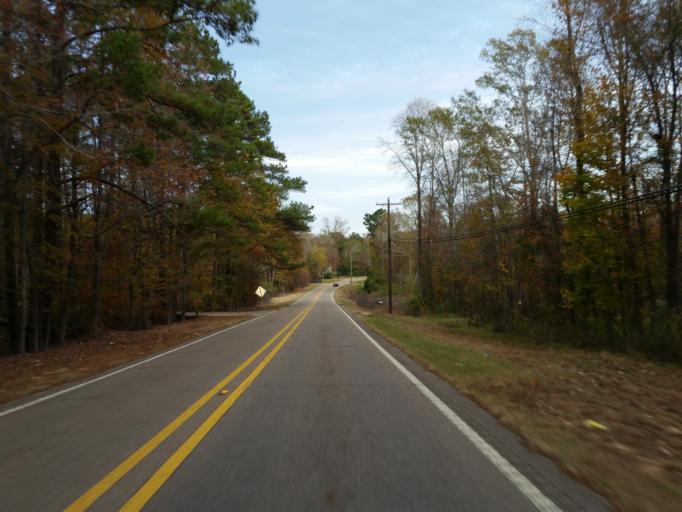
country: US
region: Mississippi
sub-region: Lauderdale County
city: Marion
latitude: 32.4105
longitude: -88.5606
